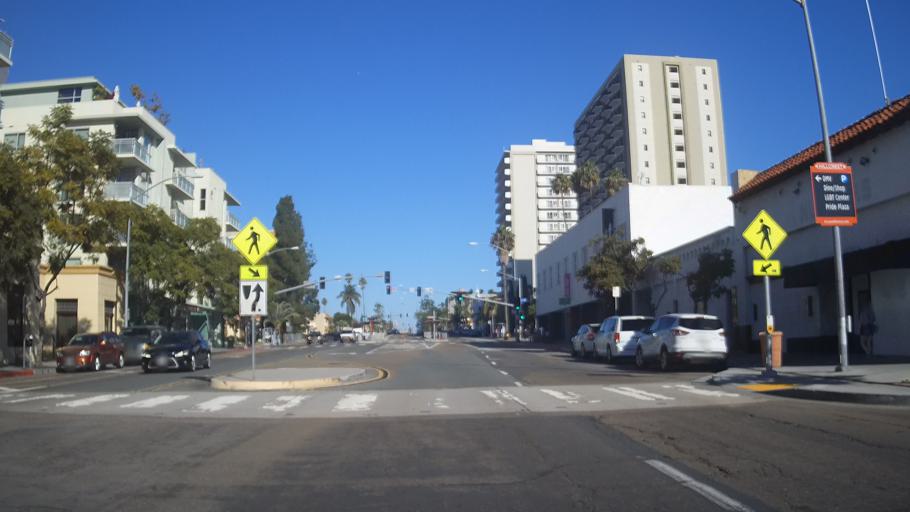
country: US
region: California
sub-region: San Diego County
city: San Diego
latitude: 32.7474
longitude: -117.1463
